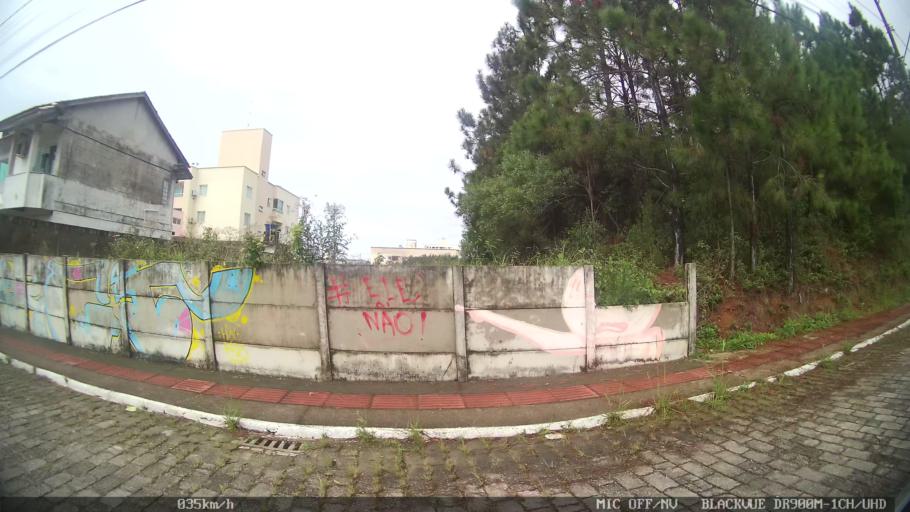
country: BR
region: Santa Catarina
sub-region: Sao Jose
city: Campinas
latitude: -27.5526
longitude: -48.6368
